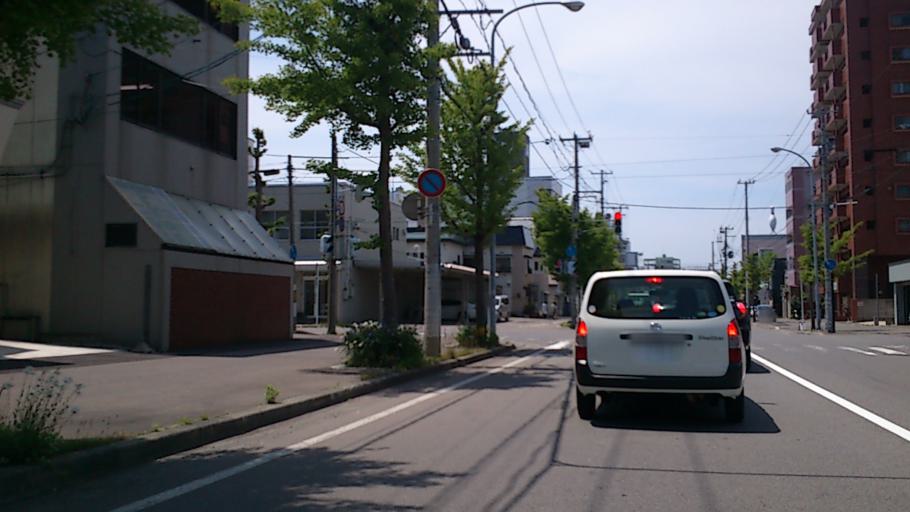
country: JP
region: Aomori
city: Aomori Shi
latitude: 40.8280
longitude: 140.7424
